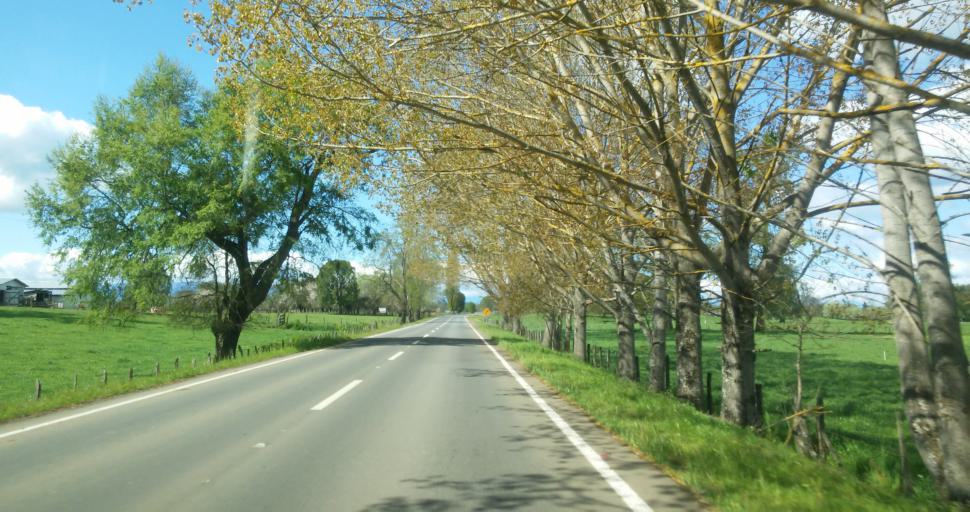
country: CL
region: Los Rios
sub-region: Provincia del Ranco
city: Rio Bueno
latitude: -40.2418
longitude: -72.6092
